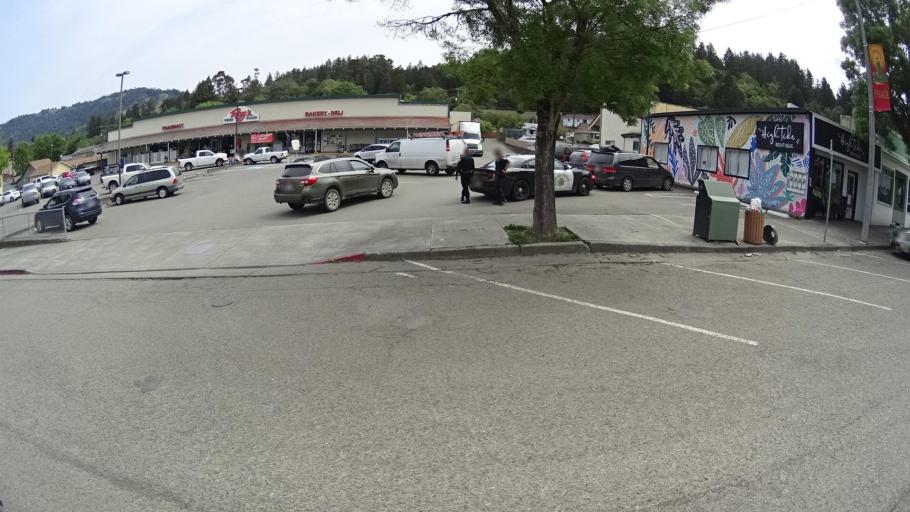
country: US
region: California
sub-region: Humboldt County
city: Redway
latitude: 40.0985
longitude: -123.7950
